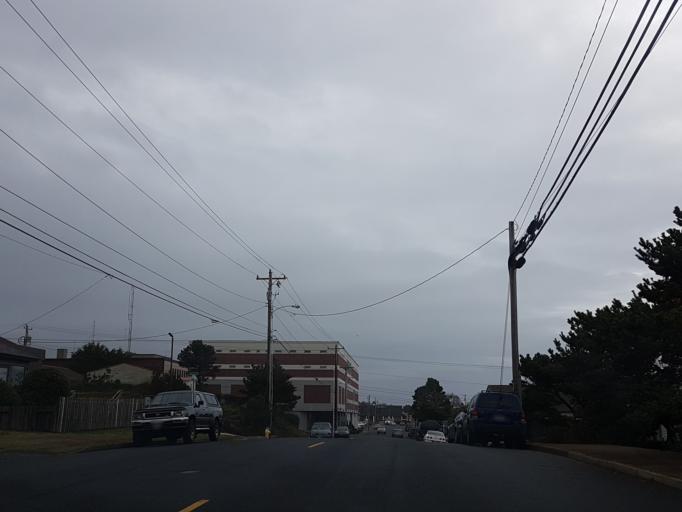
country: US
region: Oregon
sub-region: Lincoln County
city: Newport
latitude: 44.6376
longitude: -124.0557
